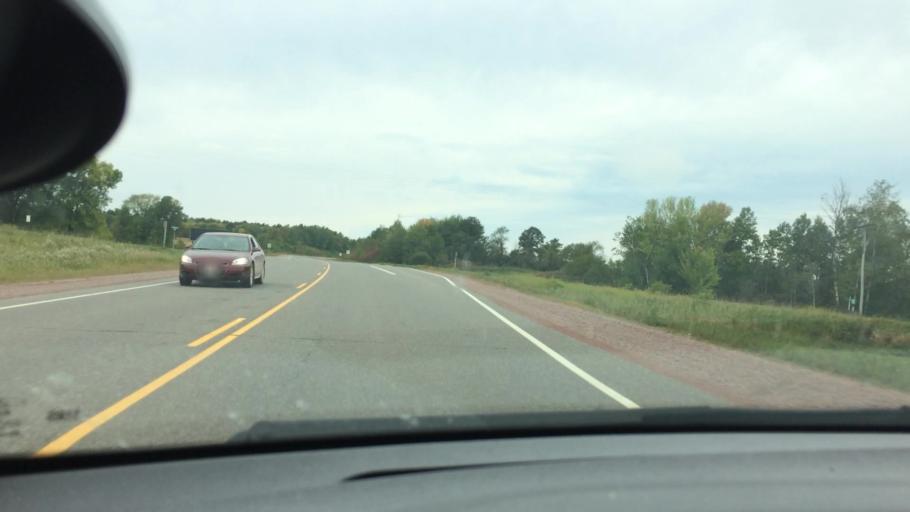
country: US
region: Wisconsin
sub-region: Clark County
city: Neillsville
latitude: 44.5522
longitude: -90.6175
